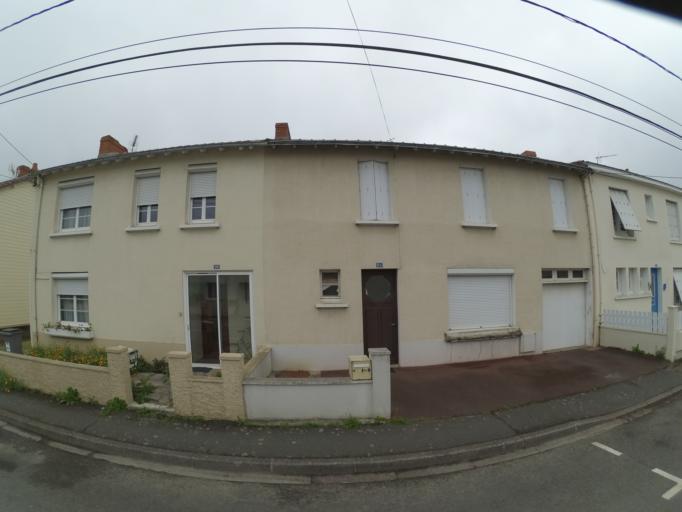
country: FR
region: Pays de la Loire
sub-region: Departement de la Vendee
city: La Roche-sur-Yon
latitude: 46.6540
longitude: -1.4329
